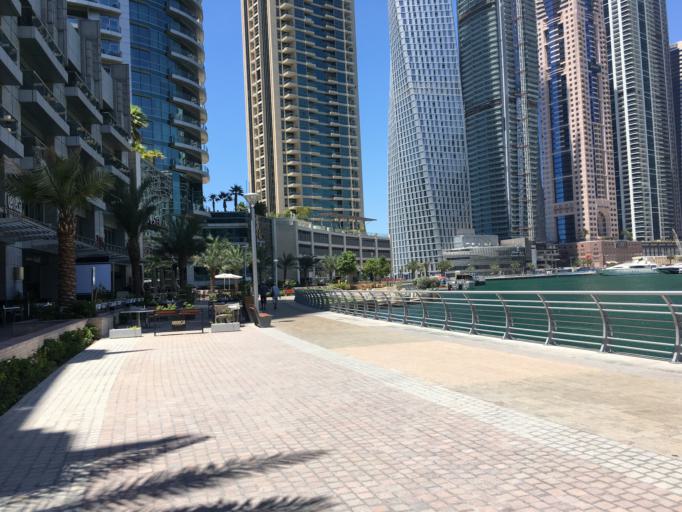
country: AE
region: Dubai
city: Dubai
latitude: 25.0837
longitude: 55.1453
